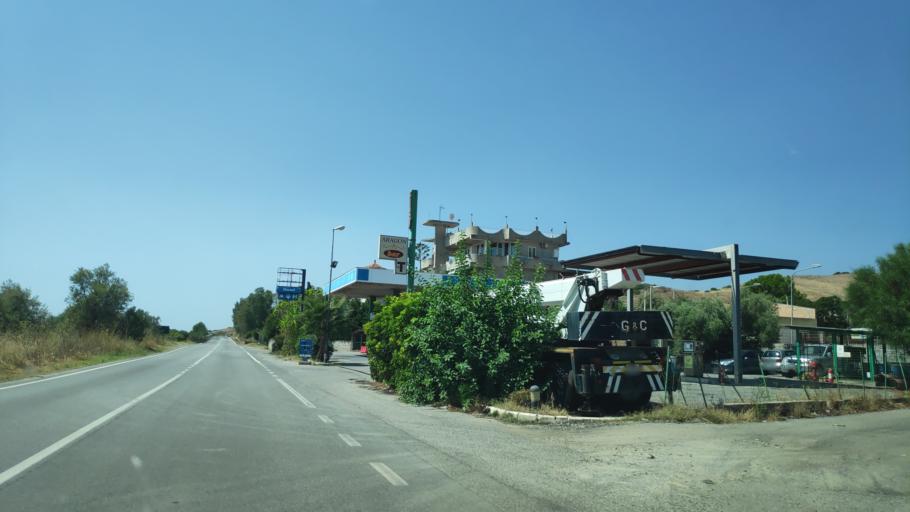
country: IT
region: Calabria
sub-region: Provincia di Reggio Calabria
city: Africo Nuovo
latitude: 38.0097
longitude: 16.1299
